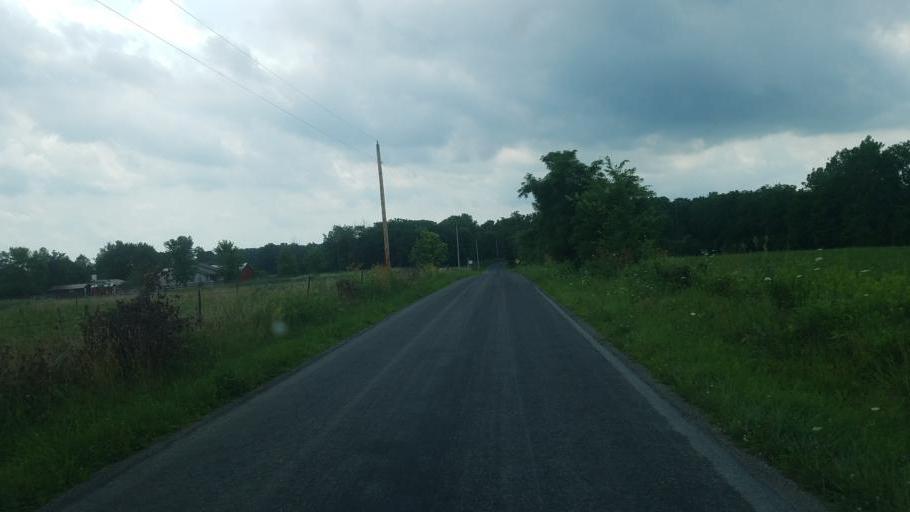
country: US
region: Ohio
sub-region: Hardin County
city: Kenton
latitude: 40.5872
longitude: -83.5698
